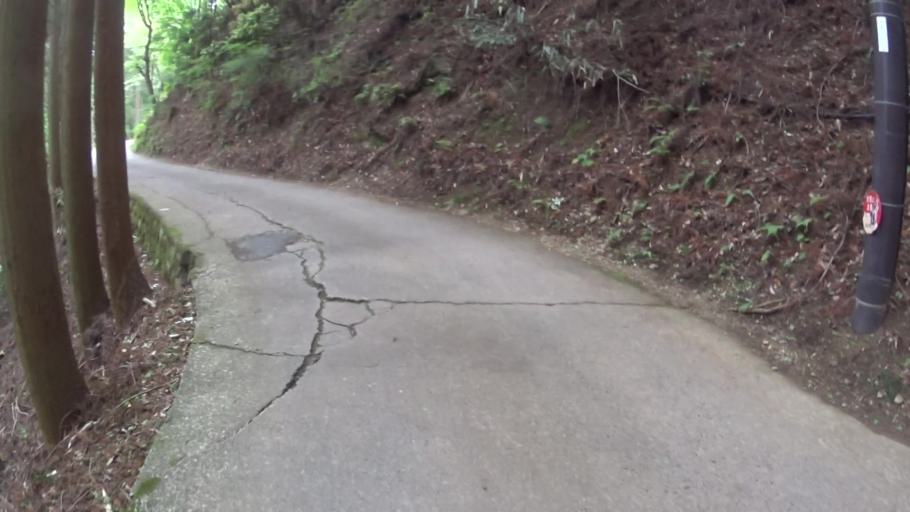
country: JP
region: Nara
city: Yoshino-cho
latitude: 34.3499
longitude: 135.8773
